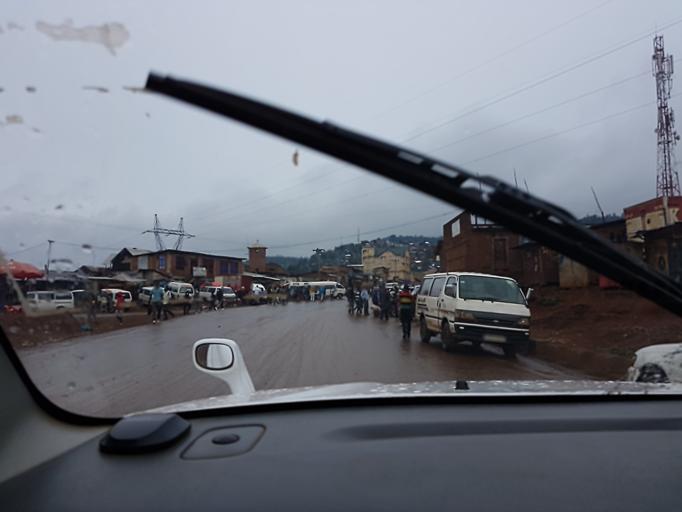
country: CD
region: South Kivu
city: Bukavu
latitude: -2.5211
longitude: 28.8549
